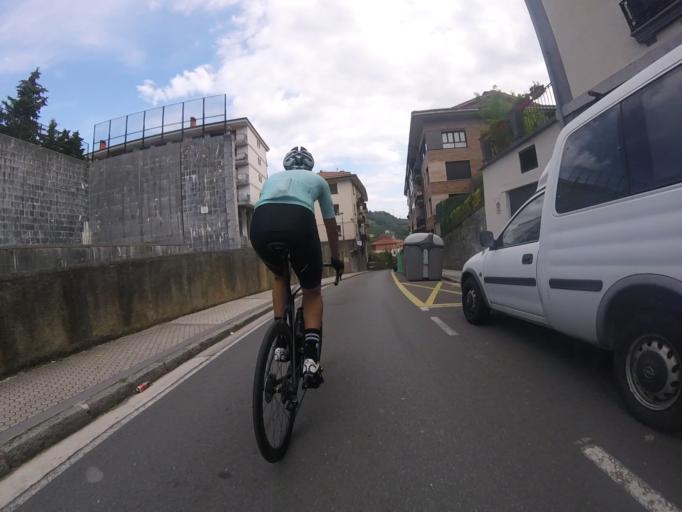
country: ES
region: Basque Country
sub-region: Provincia de Guipuzcoa
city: Andoain
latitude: 43.2201
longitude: -2.0194
